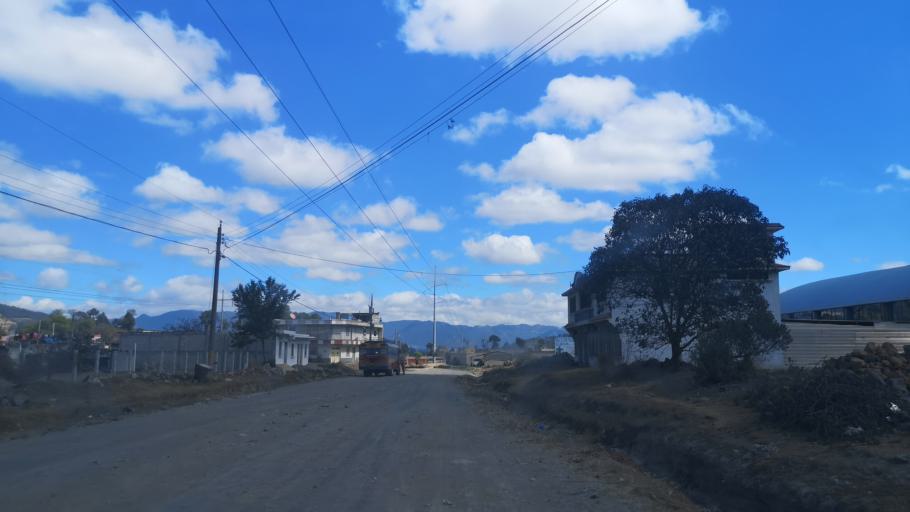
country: GT
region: Quetzaltenango
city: Almolonga
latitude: 14.7940
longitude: -91.5372
